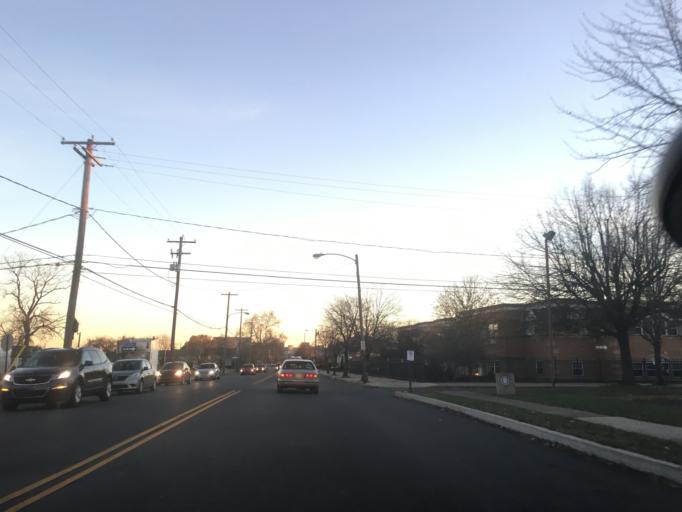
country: US
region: Pennsylvania
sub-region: Dauphin County
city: Harrisburg
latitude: 40.2800
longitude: -76.8901
